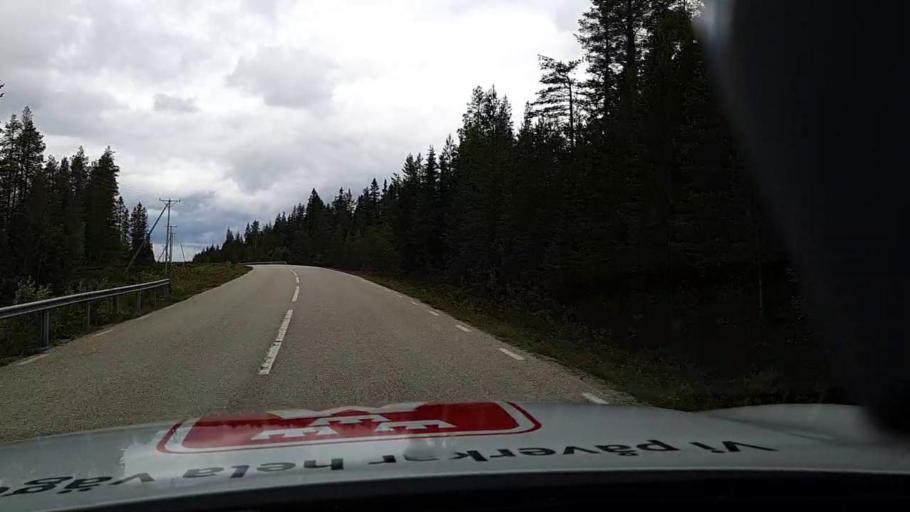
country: SE
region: Jaemtland
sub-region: Are Kommun
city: Jarpen
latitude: 62.7869
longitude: 13.6928
